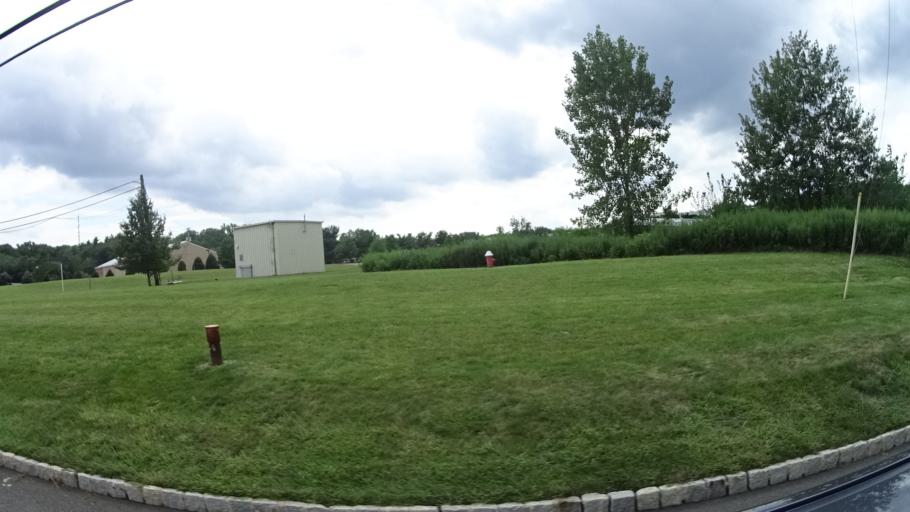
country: US
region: New Jersey
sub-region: Somerset County
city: Warren Township
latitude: 40.6324
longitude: -74.5015
